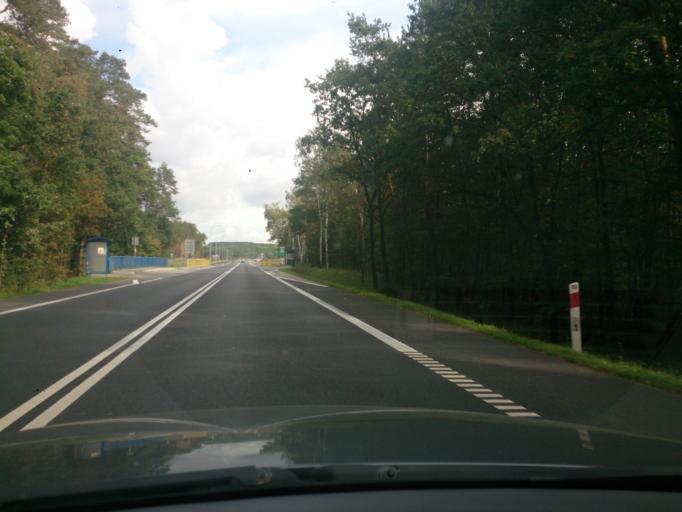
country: PL
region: Kujawsko-Pomorskie
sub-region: Powiat swiecki
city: Jezewo
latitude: 53.4584
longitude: 18.6082
